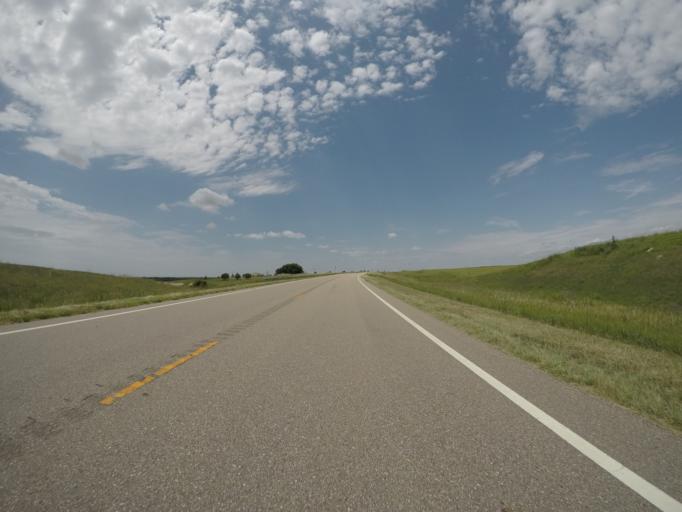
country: US
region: Kansas
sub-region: Graham County
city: Hill City
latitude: 39.3812
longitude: -99.6647
